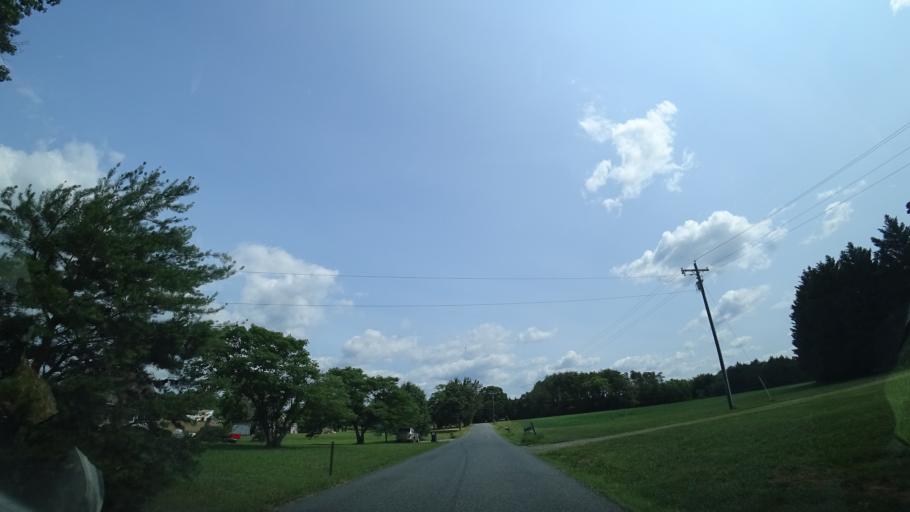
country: US
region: Virginia
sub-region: Louisa County
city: Louisa
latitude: 38.0958
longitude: -77.7992
